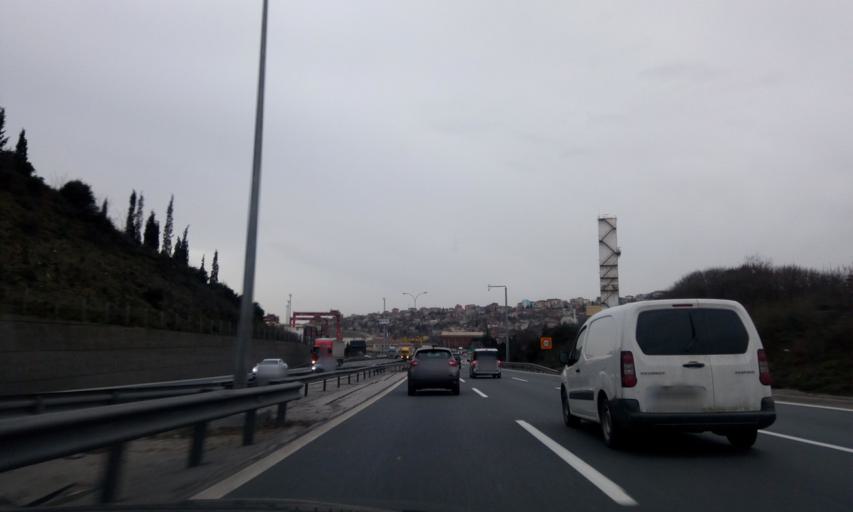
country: TR
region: Kocaeli
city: Tavsancil
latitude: 40.7765
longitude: 29.5388
